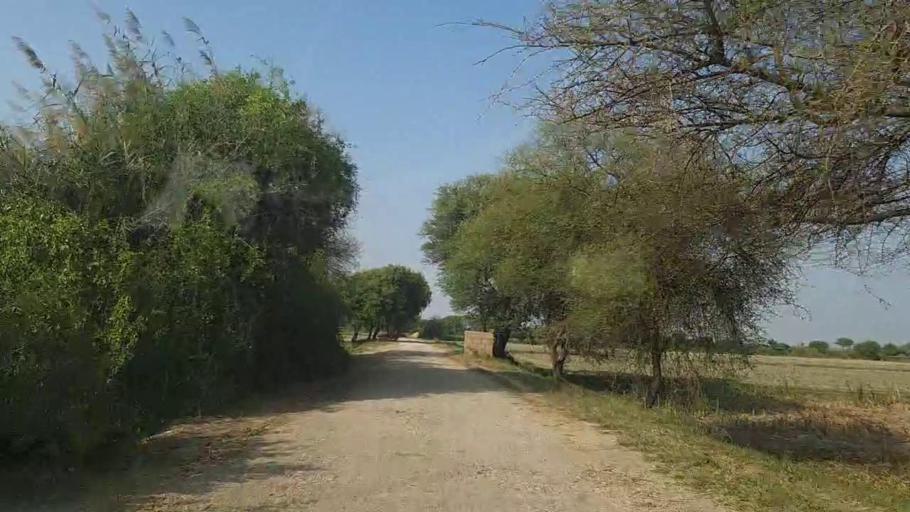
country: PK
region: Sindh
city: Mirpur Sakro
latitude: 24.5709
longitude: 67.6848
